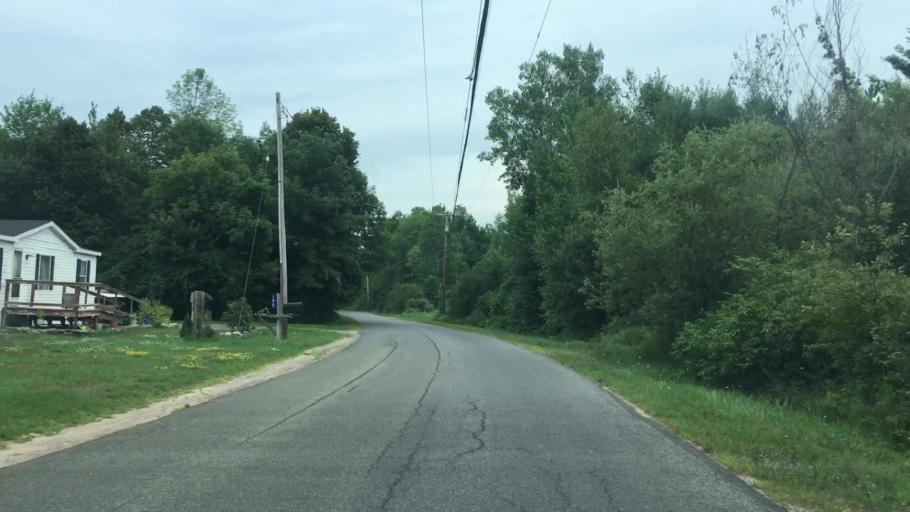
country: US
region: New York
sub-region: Clinton County
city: Peru
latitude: 44.6022
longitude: -73.6041
